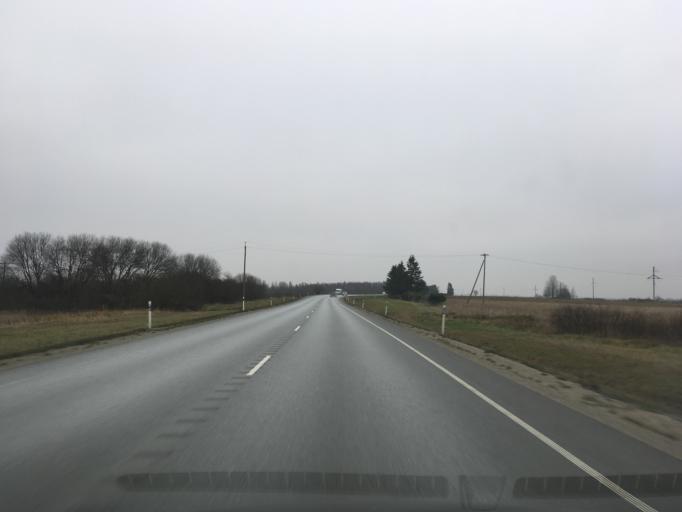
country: EE
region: Ida-Virumaa
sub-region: Kivioli linn
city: Kivioli
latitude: 59.4231
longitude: 26.9655
